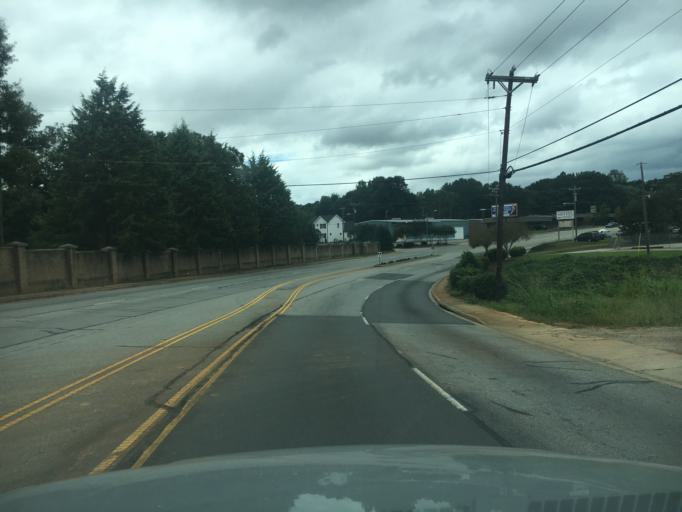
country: US
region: South Carolina
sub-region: Greenville County
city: Greenville
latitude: 34.8756
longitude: -82.3941
